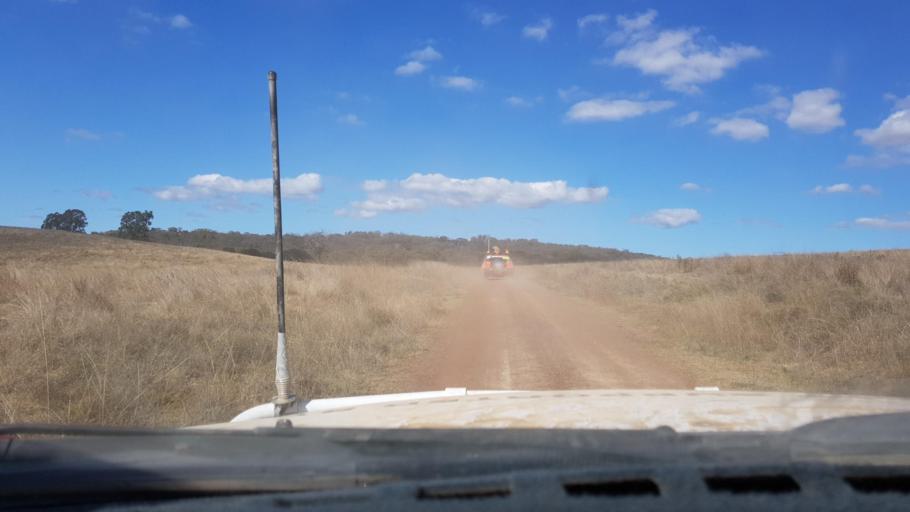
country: AU
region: New South Wales
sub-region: Tamworth Municipality
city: Manilla
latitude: -30.4419
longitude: 150.8632
